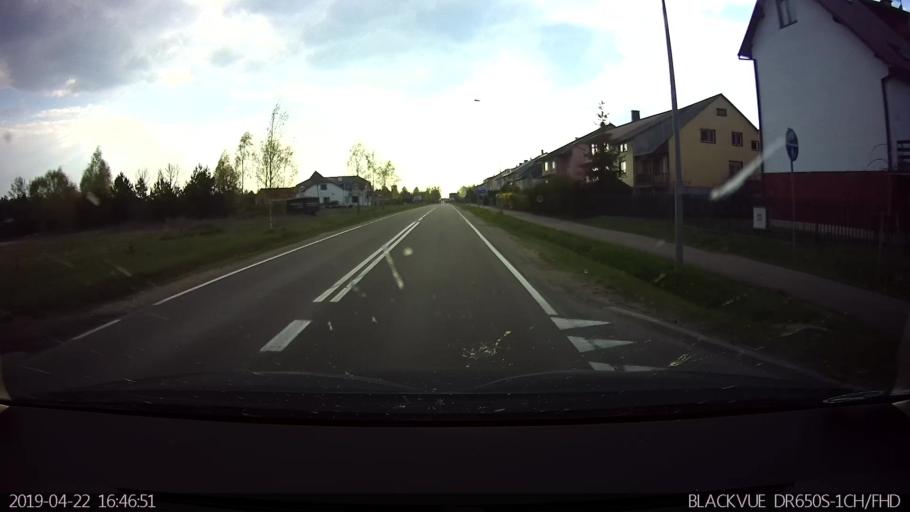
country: PL
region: Podlasie
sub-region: Powiat siemiatycki
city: Siemiatycze
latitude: 52.4341
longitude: 22.8940
